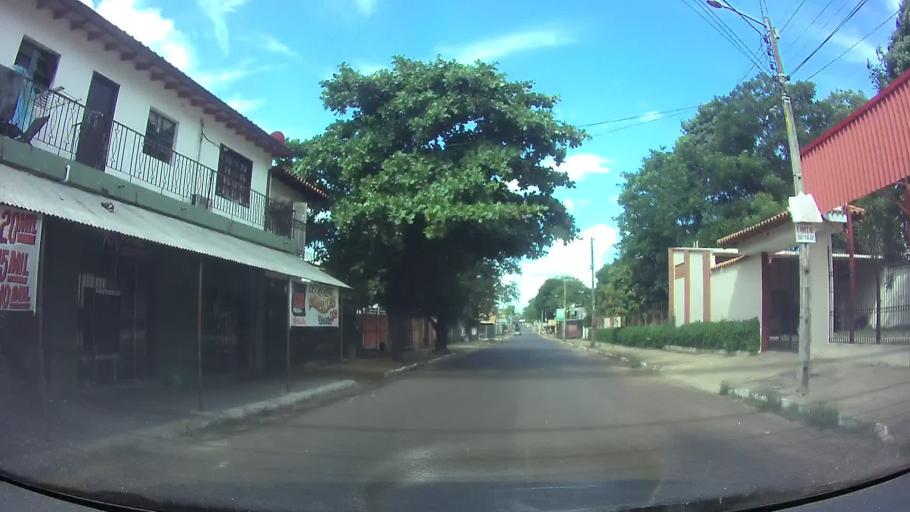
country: PY
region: Central
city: Villa Elisa
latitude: -25.3423
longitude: -57.5759
